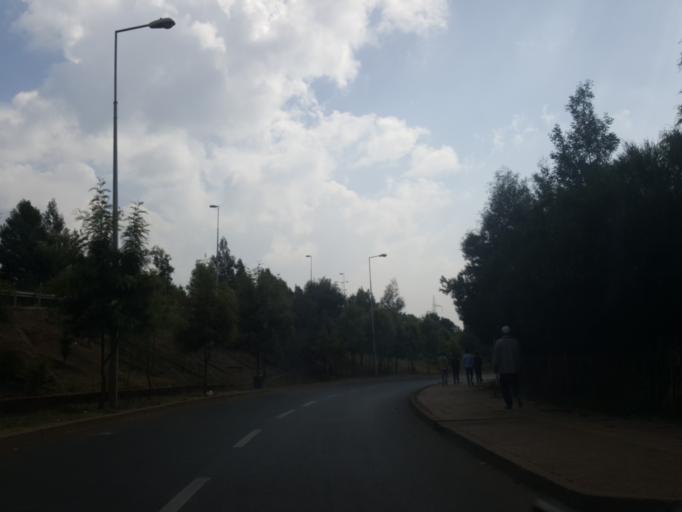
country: ET
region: Adis Abeba
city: Addis Ababa
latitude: 9.0695
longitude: 38.7199
